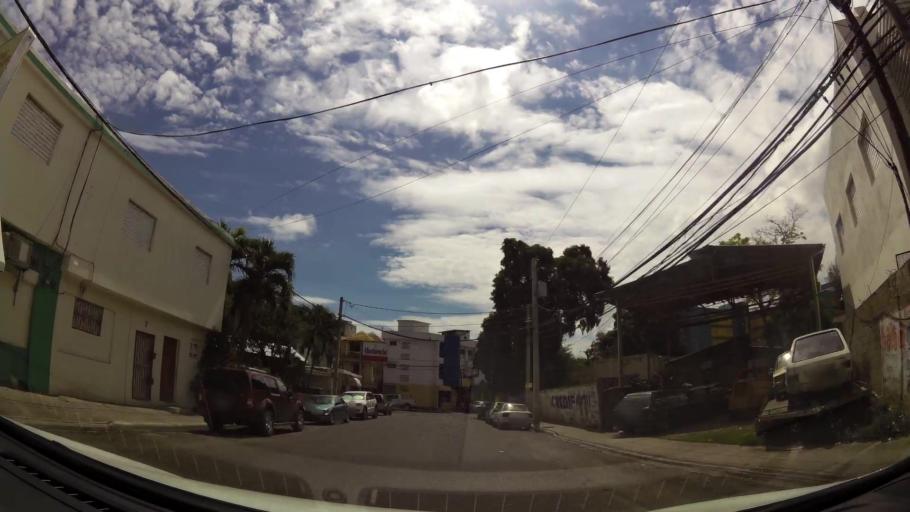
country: DO
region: Santiago
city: Santiago de los Caballeros
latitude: 19.4577
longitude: -70.6999
